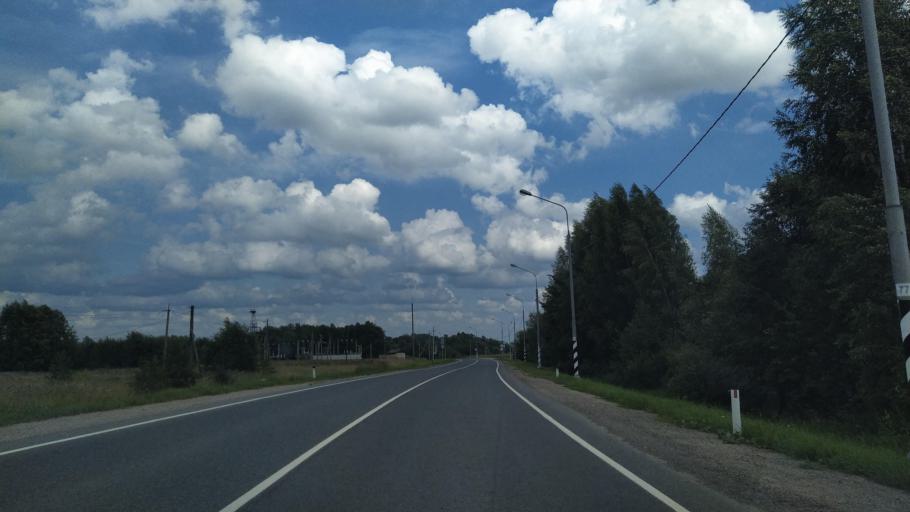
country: RU
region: Pskov
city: Dno
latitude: 58.0591
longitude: 29.9702
